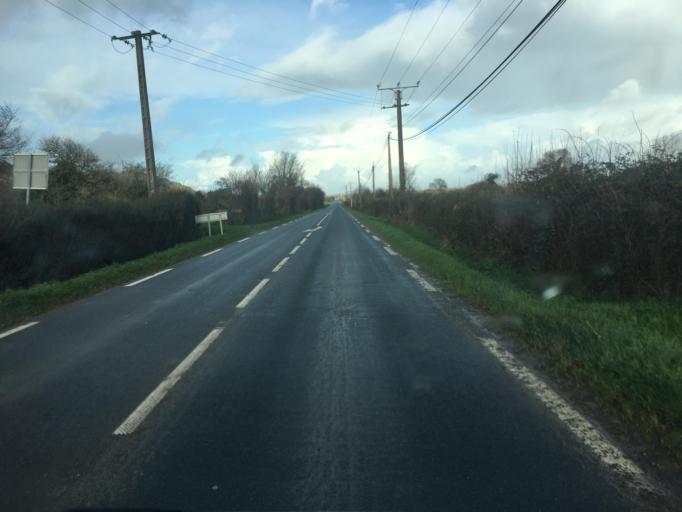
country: FR
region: Lower Normandy
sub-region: Departement de la Manche
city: Quettehou
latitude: 49.6063
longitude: -1.2932
